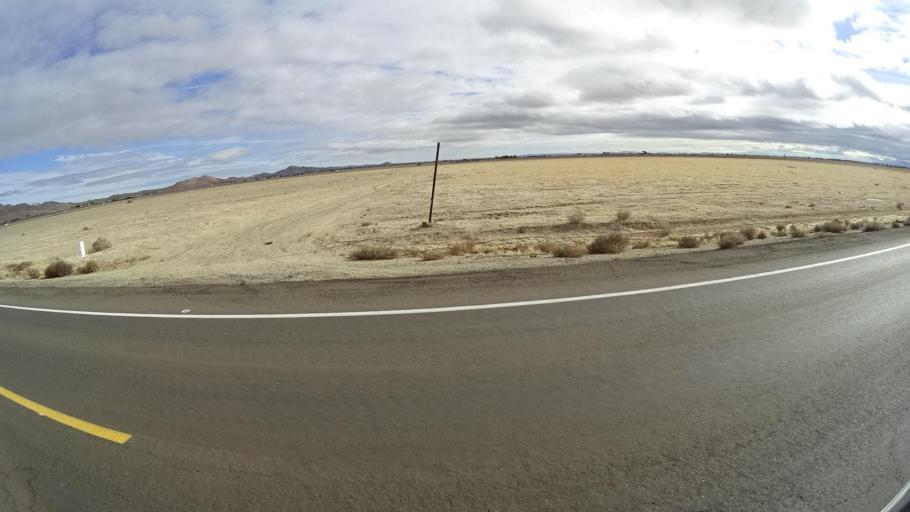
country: US
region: California
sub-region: Kern County
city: Rosamond
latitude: 34.8490
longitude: -118.2909
